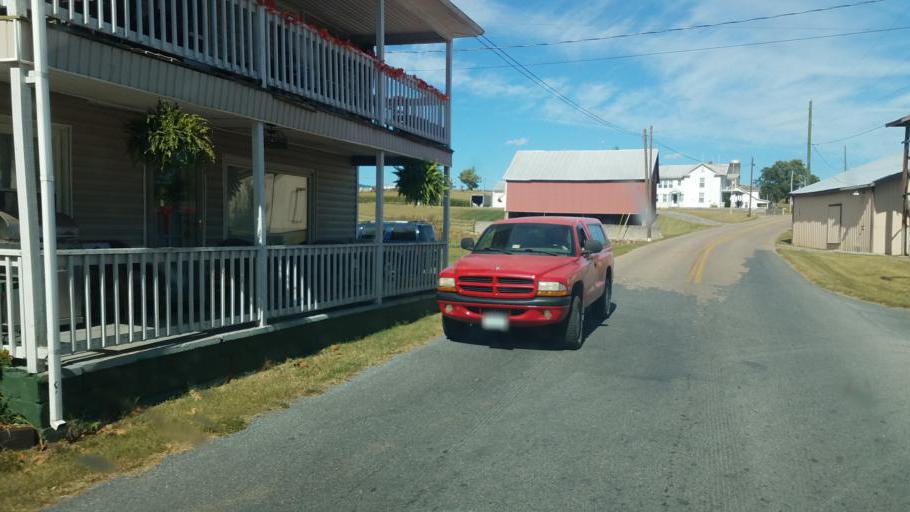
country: US
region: Virginia
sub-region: Page County
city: Stanley
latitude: 38.5915
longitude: -78.5576
